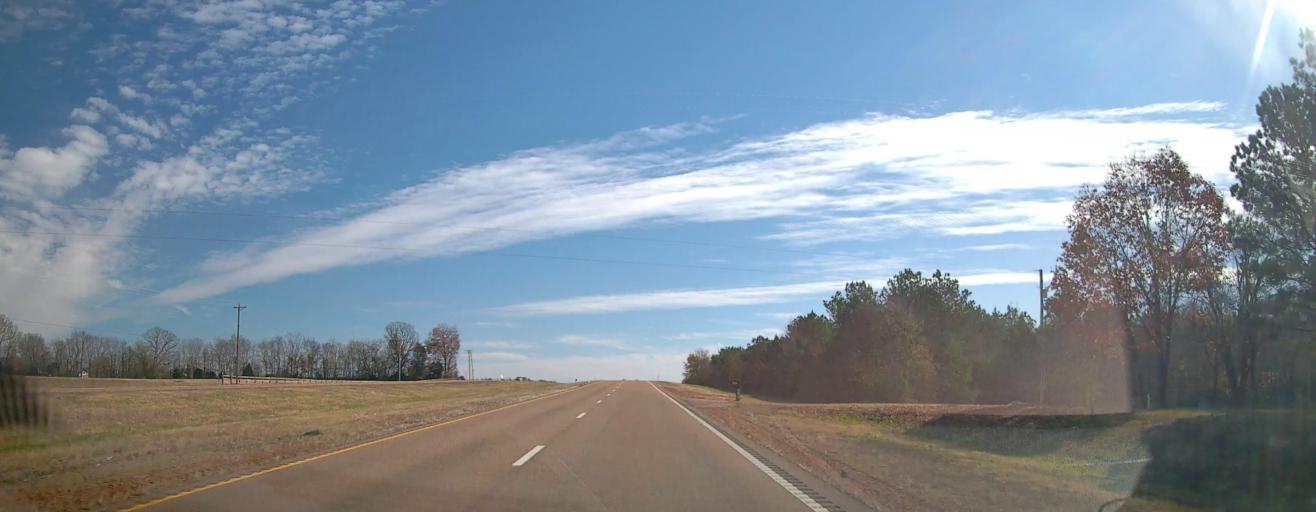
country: US
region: Tennessee
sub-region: Fayette County
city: Piperton
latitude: 34.9710
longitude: -89.5583
